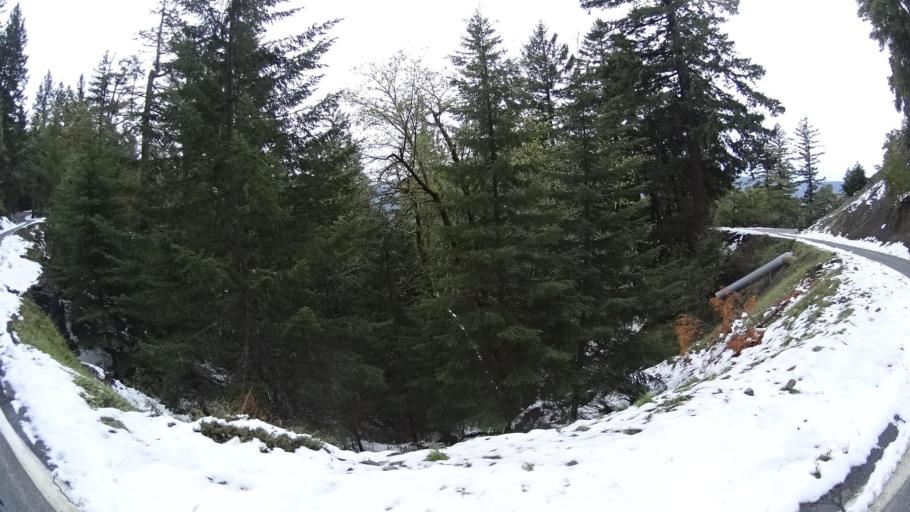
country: US
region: California
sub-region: Humboldt County
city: Willow Creek
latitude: 40.8791
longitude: -123.7580
